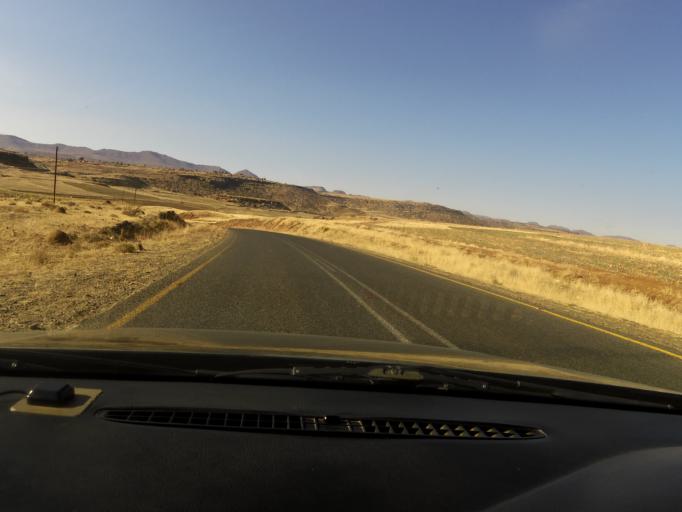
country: LS
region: Mohale's Hoek District
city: Mohale's Hoek
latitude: -30.0872
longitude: 27.4301
